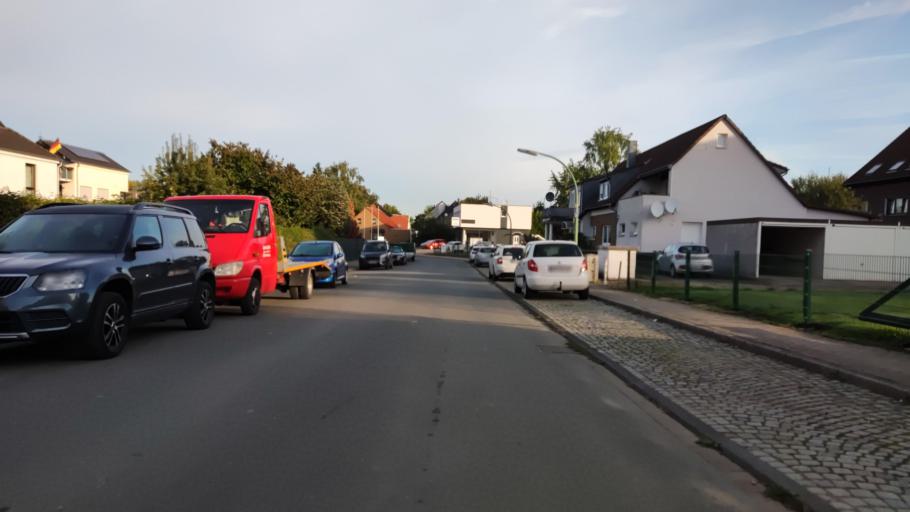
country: DE
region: North Rhine-Westphalia
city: Castrop-Rauxel
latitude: 51.5509
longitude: 7.2846
